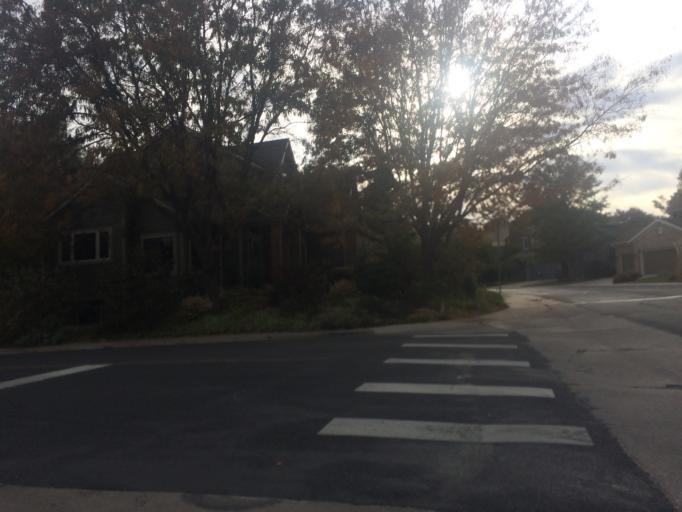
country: US
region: Colorado
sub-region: Boulder County
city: Louisville
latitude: 39.9940
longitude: -105.1181
